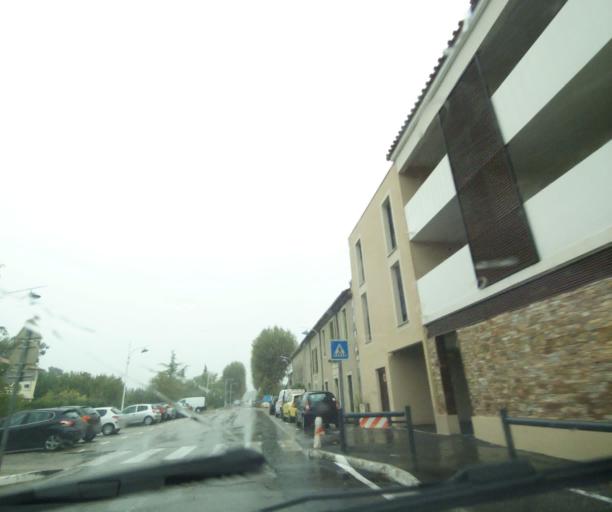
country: FR
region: Languedoc-Roussillon
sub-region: Departement du Gard
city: Milhaud
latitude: 43.7951
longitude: 4.3119
